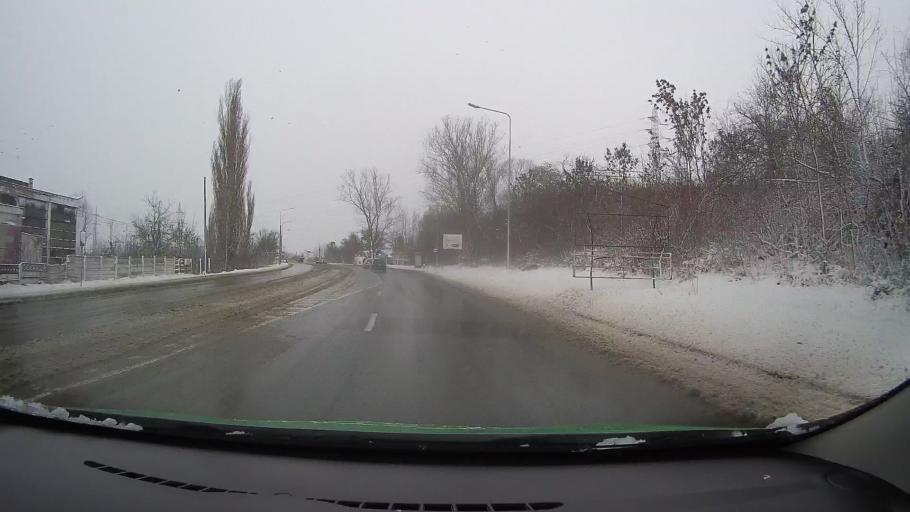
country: RO
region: Hunedoara
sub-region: Municipiul Hunedoara
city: Pestisu Mare
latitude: 45.7864
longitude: 22.9112
